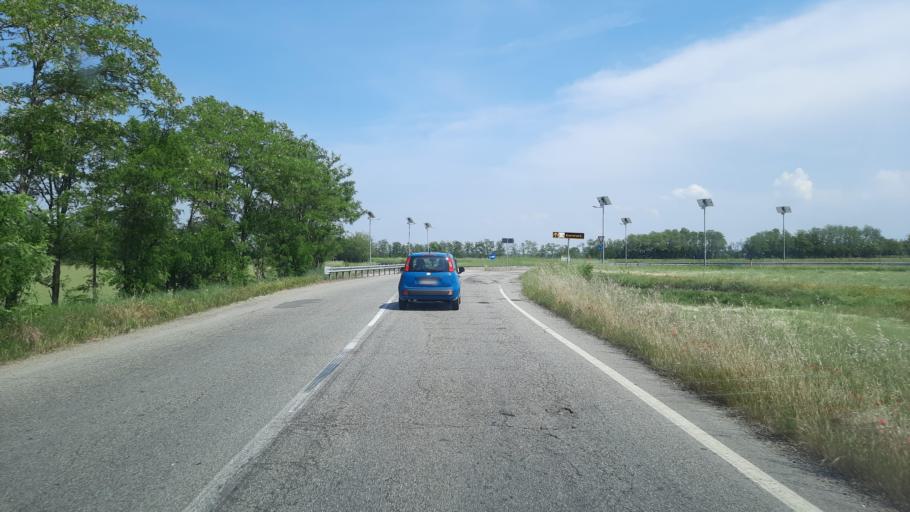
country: IT
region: Lombardy
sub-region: Provincia di Pavia
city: Cava Manara
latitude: 45.1567
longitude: 9.0925
